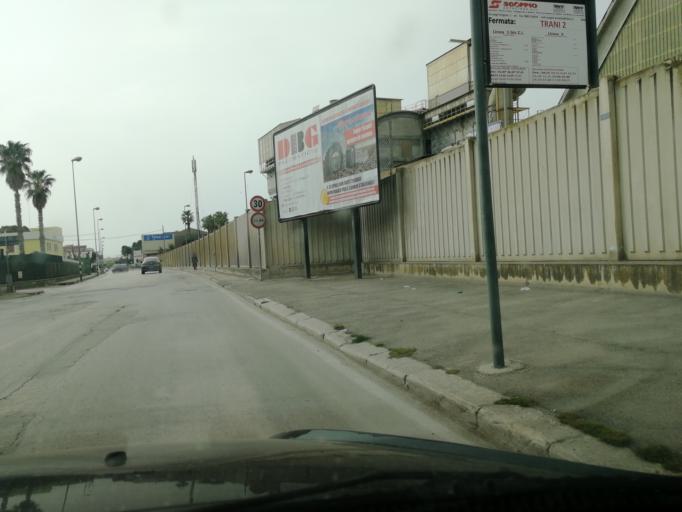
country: IT
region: Apulia
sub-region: Provincia di Barletta - Andria - Trani
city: Barletta
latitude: 41.3165
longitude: 16.2974
